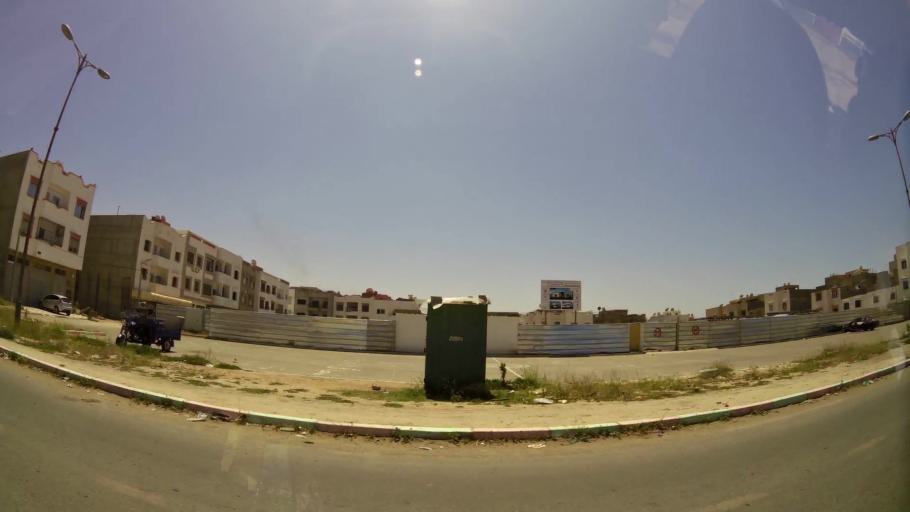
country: MA
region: Oued ed Dahab-Lagouira
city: Dakhla
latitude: 30.4313
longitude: -9.5542
